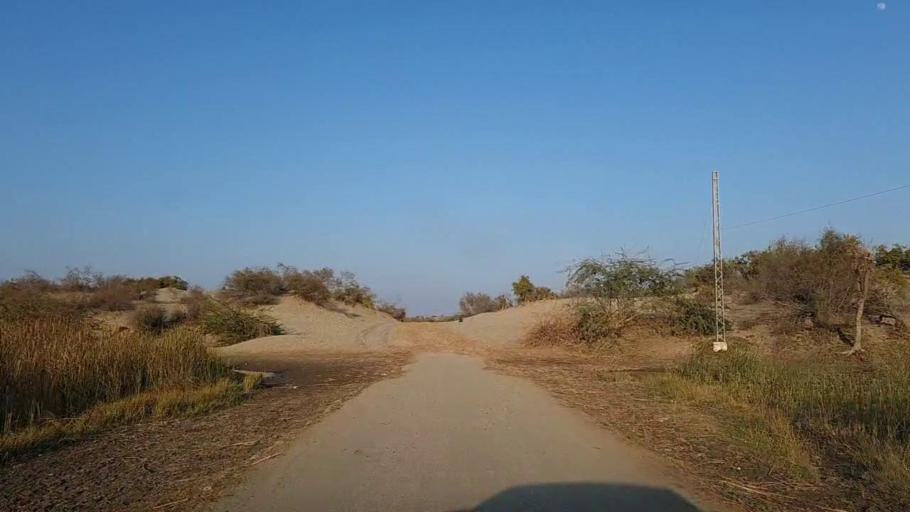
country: PK
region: Sindh
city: Sanghar
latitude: 26.3011
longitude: 68.9923
